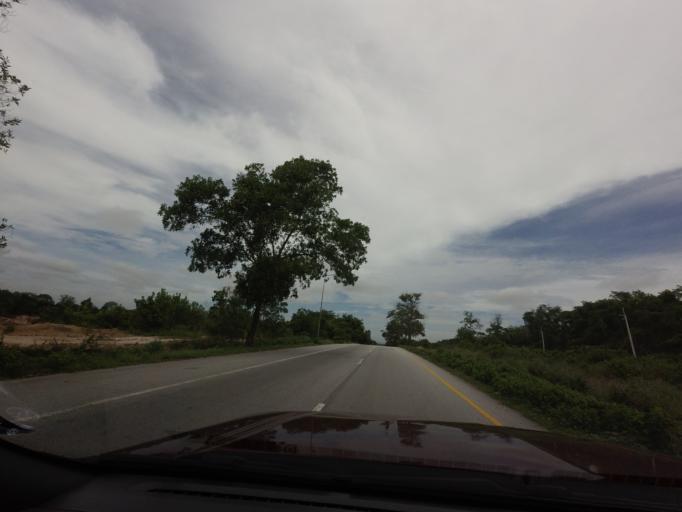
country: TH
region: Narathiwat
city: Narathiwat
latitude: 6.3458
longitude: 101.8528
